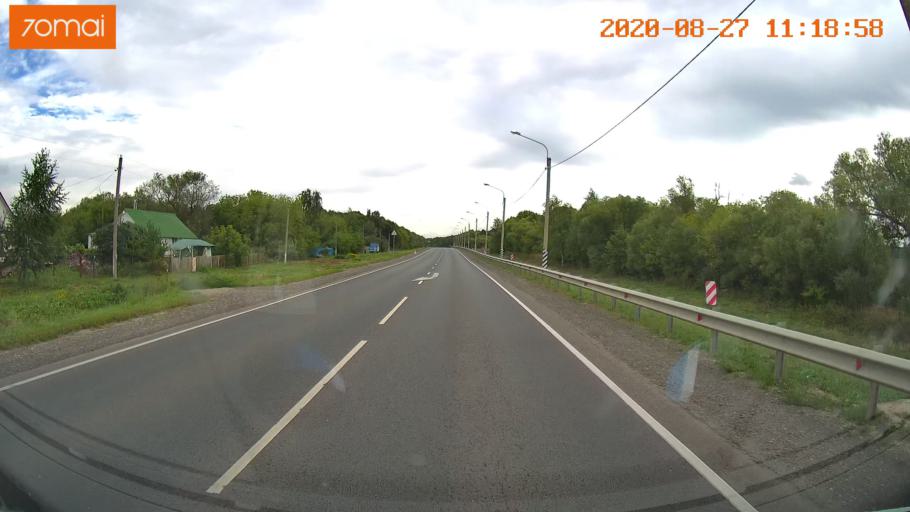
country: RU
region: Rjazan
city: Oktyabr'skiy
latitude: 54.1809
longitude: 38.9076
